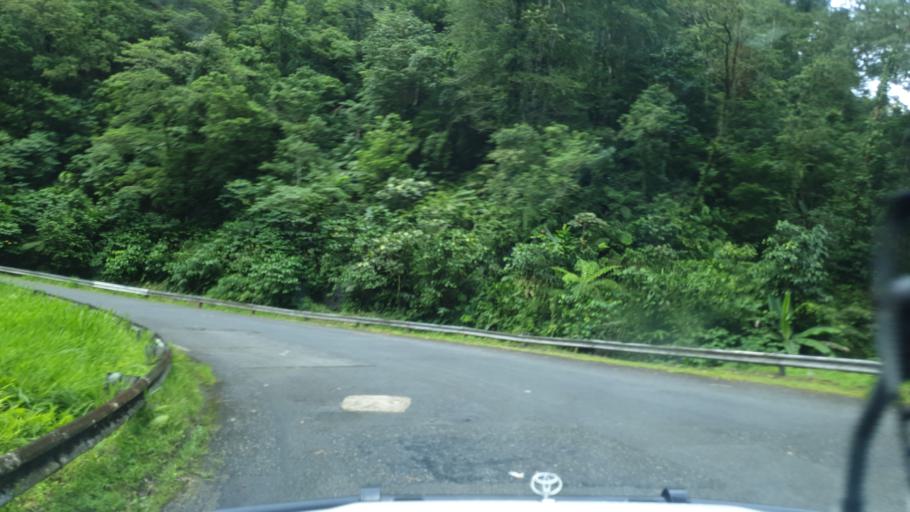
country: PG
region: Bougainville
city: Panguna
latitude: -6.2871
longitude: 155.4643
